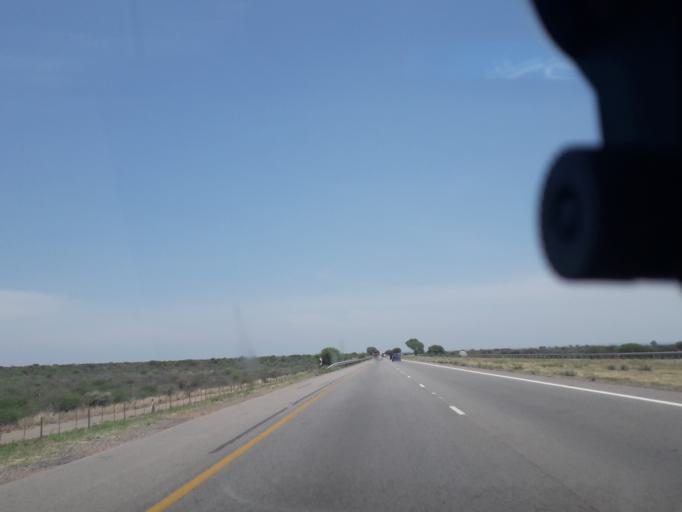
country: ZA
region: North-West
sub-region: Bojanala Platinum District Municipality
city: Makapanstad
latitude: -25.1743
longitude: 28.3069
